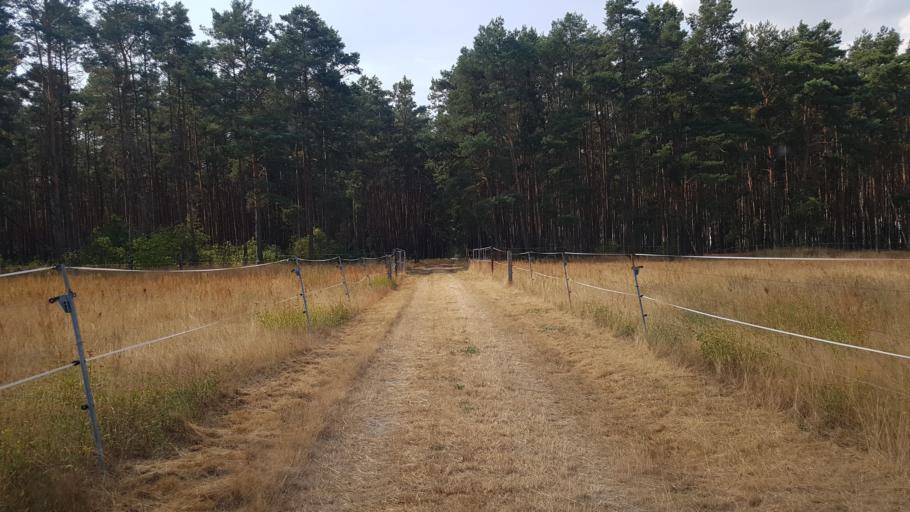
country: DE
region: Brandenburg
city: Finsterwalde
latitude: 51.6549
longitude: 13.7460
